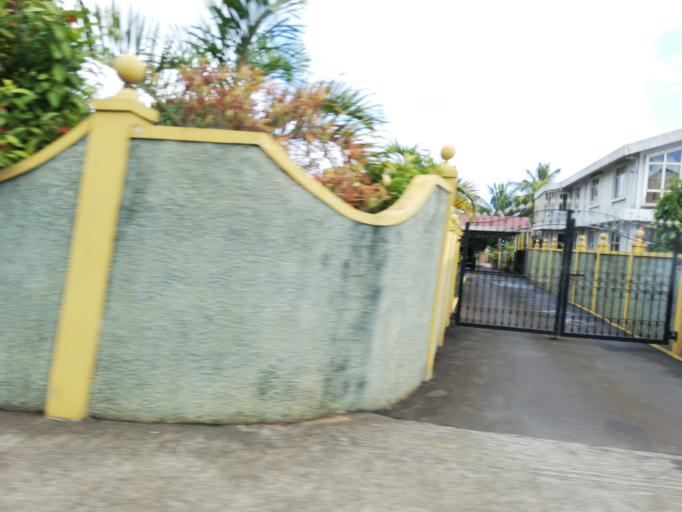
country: MU
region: Pamplemousses
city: Morcellemont Saint Andre
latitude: -20.0652
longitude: 57.5502
